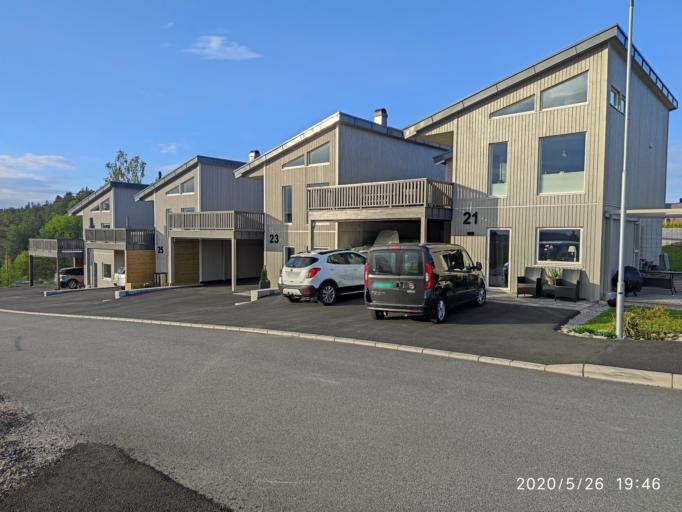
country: NO
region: Ostfold
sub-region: Halden
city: Halden
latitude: 59.1077
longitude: 11.4391
